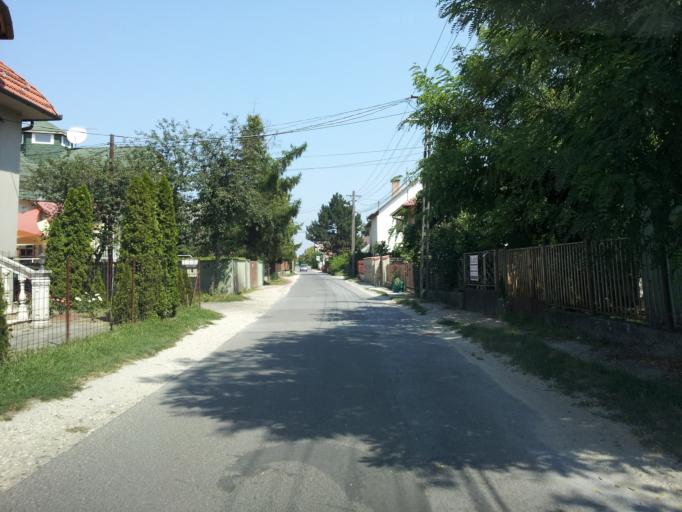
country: HU
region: Pest
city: Szigetszentmiklos
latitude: 47.3238
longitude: 19.0416
